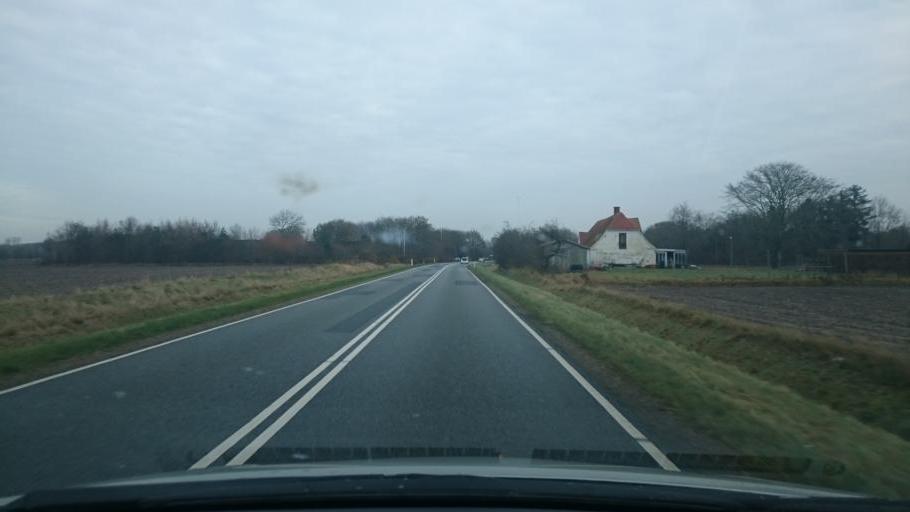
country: DK
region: South Denmark
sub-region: Esbjerg Kommune
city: Ribe
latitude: 55.3327
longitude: 8.8801
